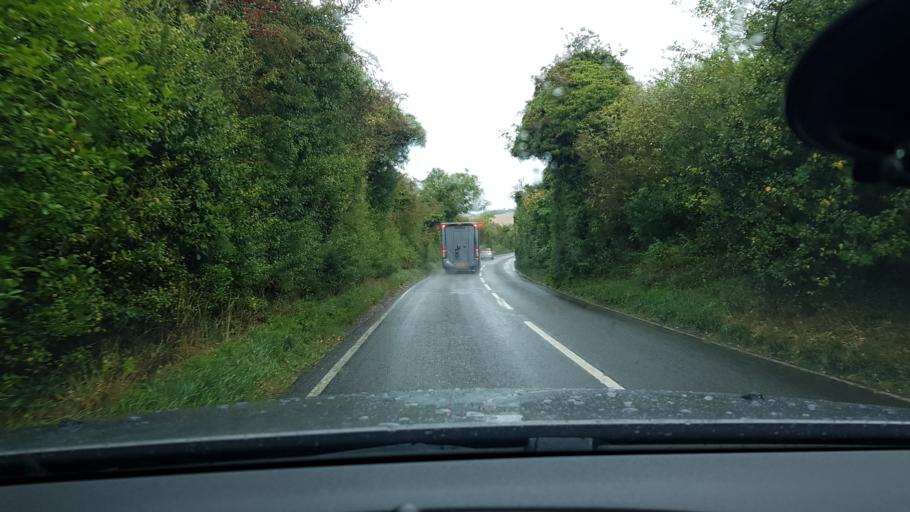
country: GB
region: England
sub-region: West Berkshire
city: Lambourn
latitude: 51.5024
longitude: -1.5378
